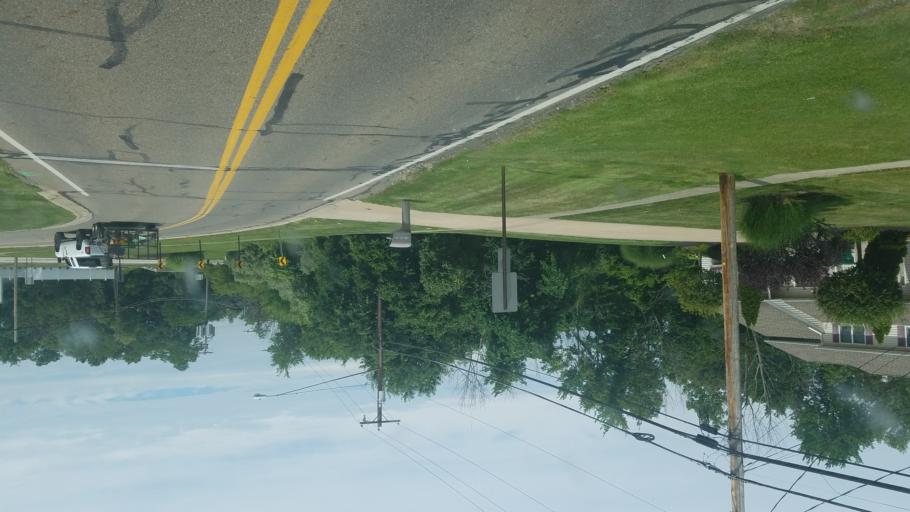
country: US
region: Ohio
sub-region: Cuyahoga County
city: Oakwood
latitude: 41.3403
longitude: -81.4789
